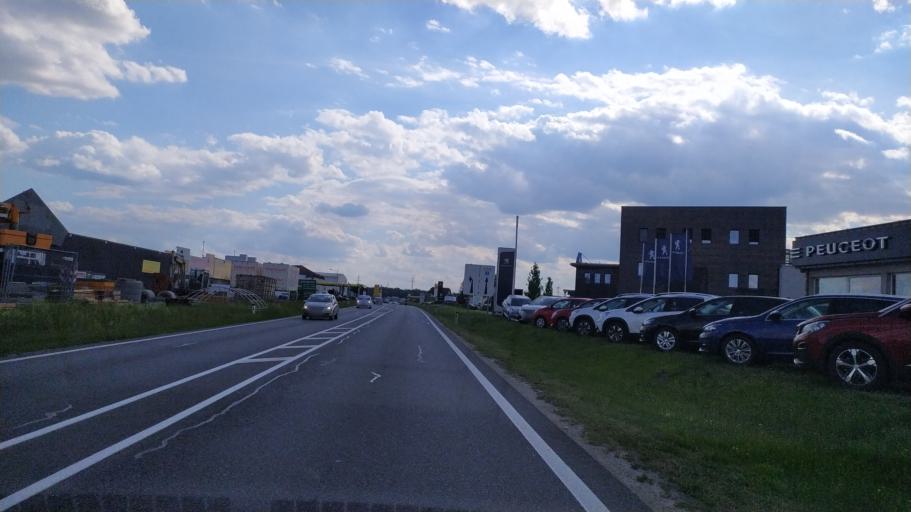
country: AT
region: Lower Austria
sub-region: Politischer Bezirk Amstetten
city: Ennsdorf
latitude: 48.2445
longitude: 14.5500
